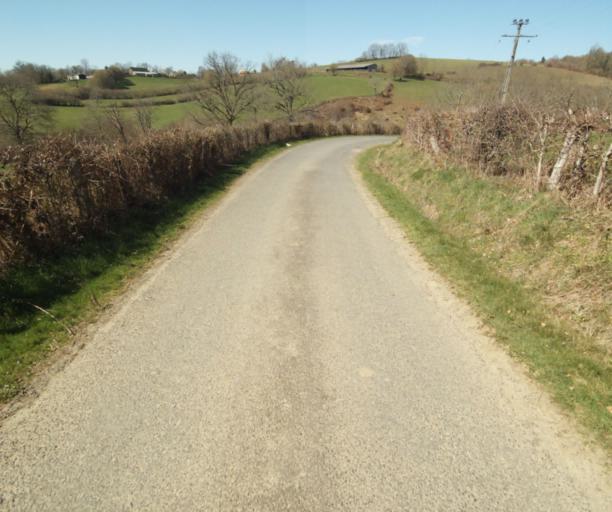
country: FR
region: Limousin
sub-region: Departement de la Correze
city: Chamboulive
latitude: 45.4495
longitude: 1.6734
